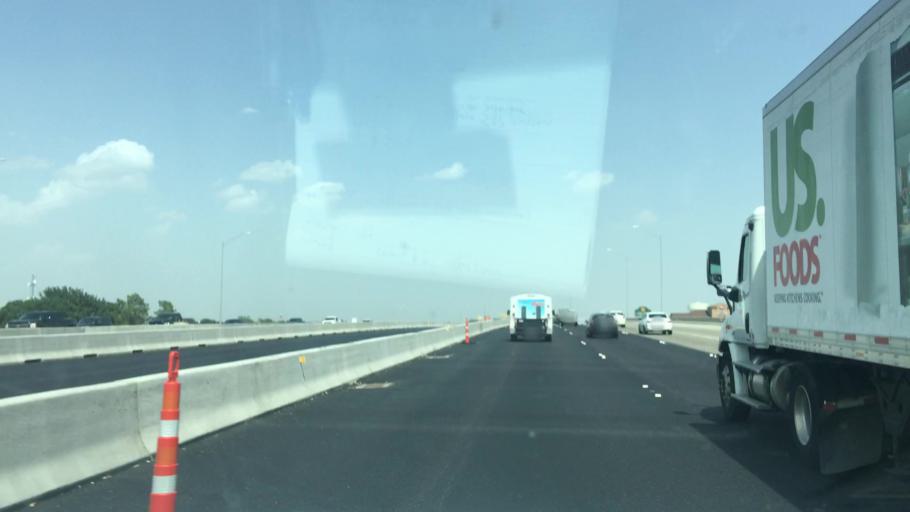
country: US
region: Texas
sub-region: Tarrant County
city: Euless
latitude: 32.8375
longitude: -97.0939
